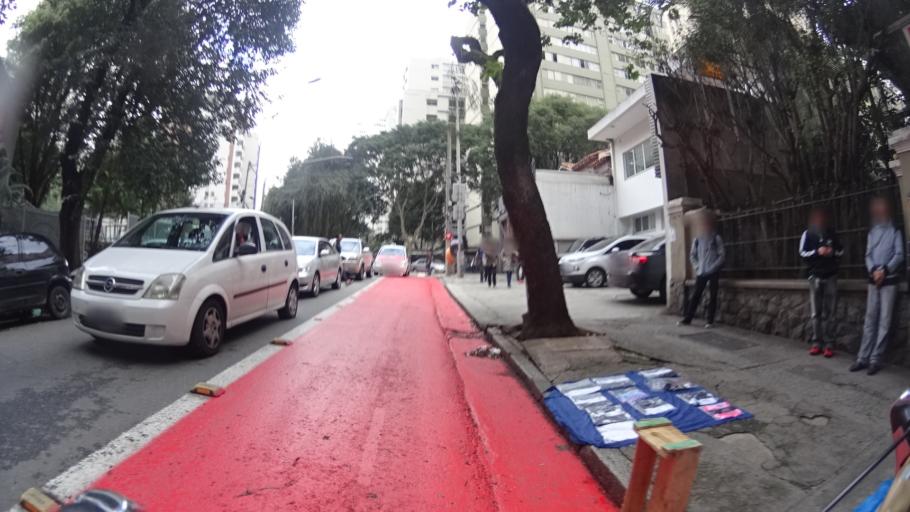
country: BR
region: Sao Paulo
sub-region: Sao Paulo
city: Sao Paulo
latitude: -23.5359
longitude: -46.6569
